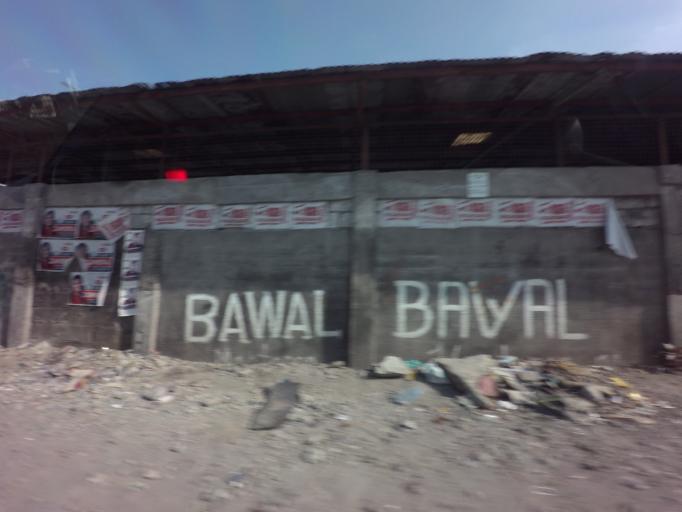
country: PH
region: Calabarzon
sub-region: Province of Rizal
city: Taguig
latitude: 14.4987
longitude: 121.0556
